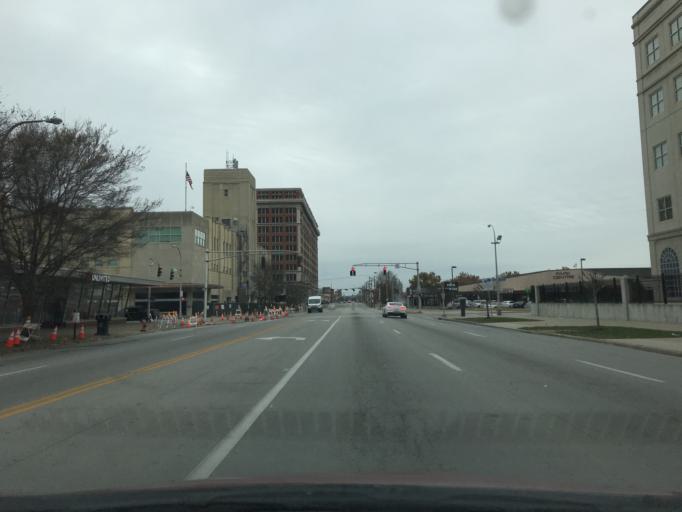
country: US
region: Kentucky
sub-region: Jefferson County
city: Louisville
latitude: 38.2466
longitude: -85.7643
